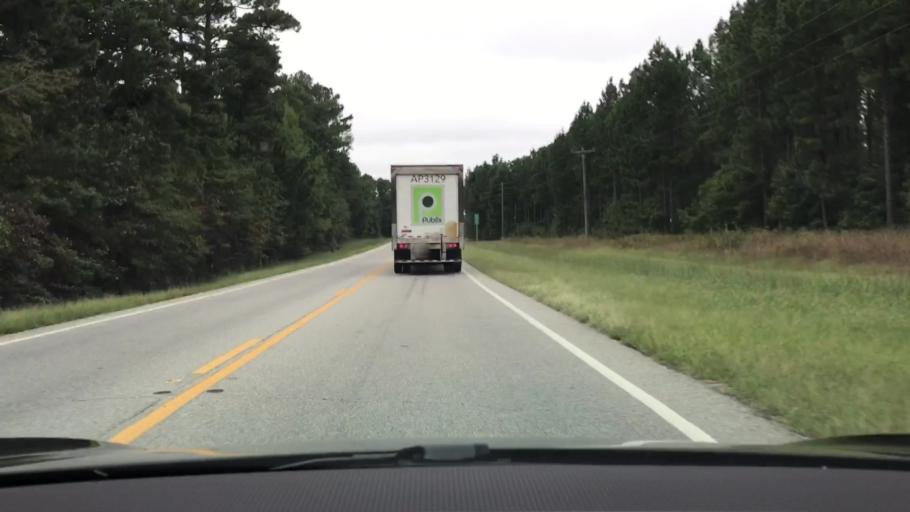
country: US
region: Georgia
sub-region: Greene County
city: Greensboro
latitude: 33.6655
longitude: -83.2505
